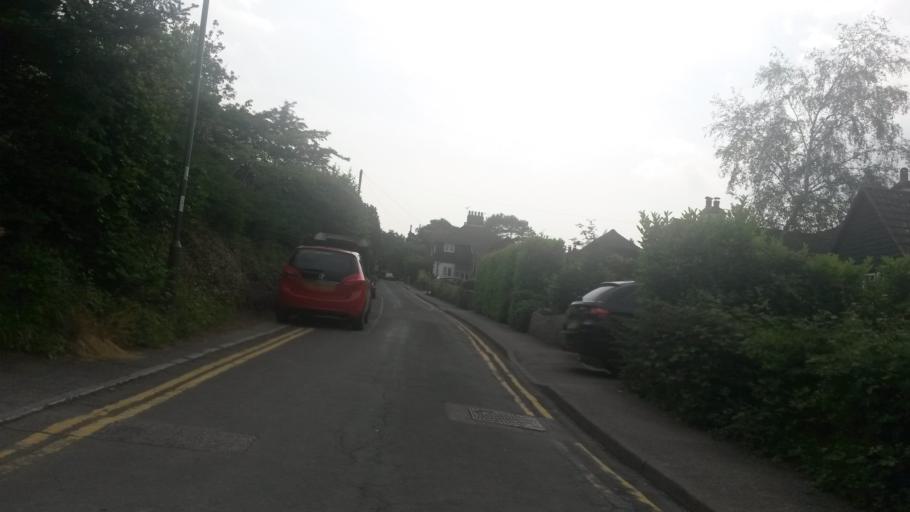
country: GB
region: England
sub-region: Surrey
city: Haslemere
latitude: 51.0871
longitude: -0.7213
